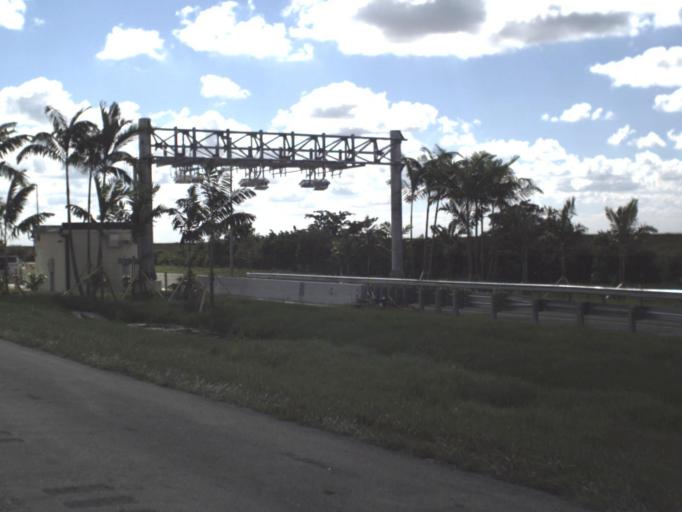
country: US
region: Florida
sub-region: Broward County
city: Coral Springs
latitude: 26.2765
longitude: -80.2970
